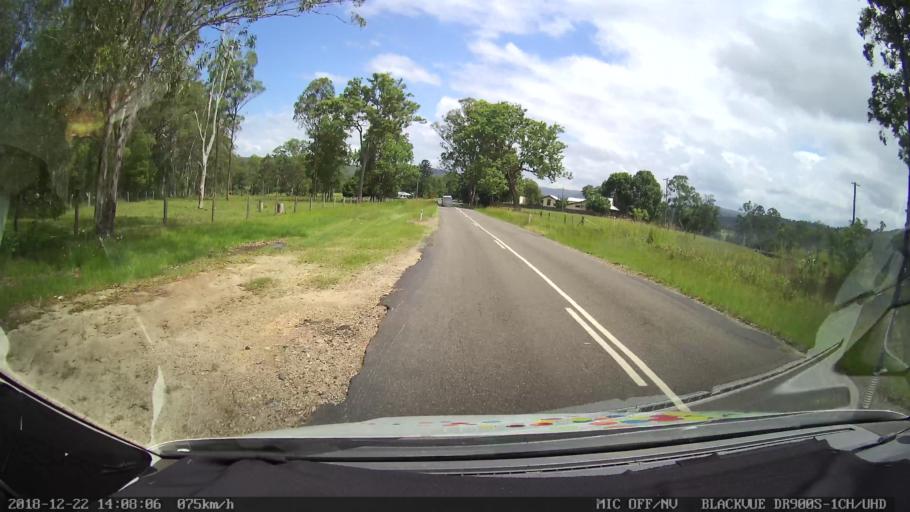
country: AU
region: New South Wales
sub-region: Clarence Valley
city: Coutts Crossing
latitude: -29.9749
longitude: 152.7258
